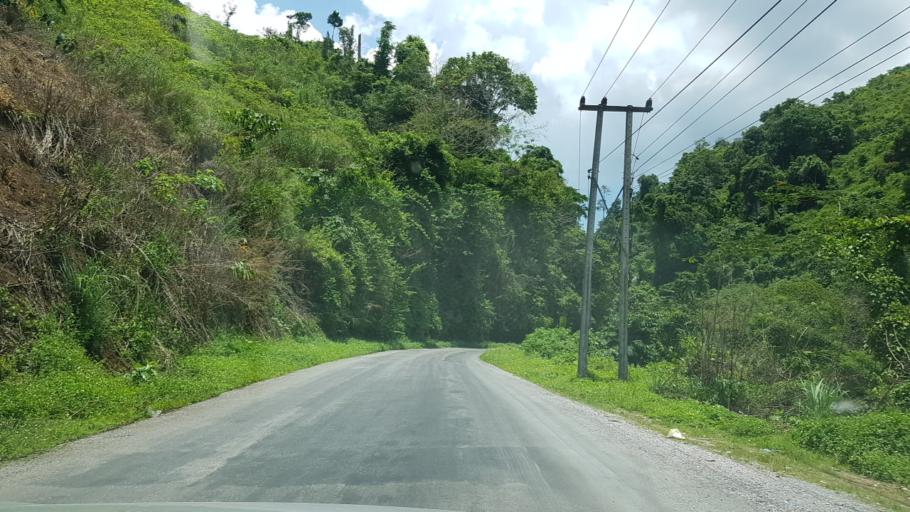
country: LA
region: Vientiane
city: Muang Kasi
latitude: 19.1388
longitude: 102.2928
